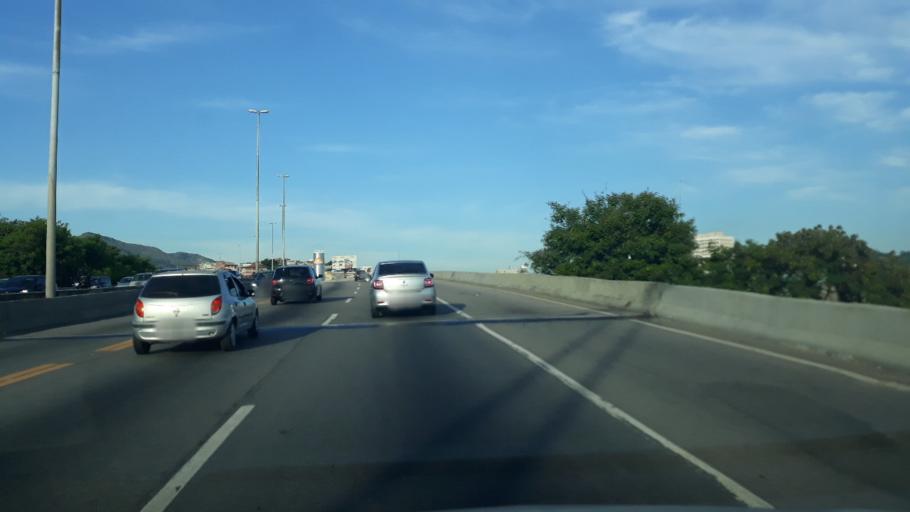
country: BR
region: Rio de Janeiro
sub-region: Rio De Janeiro
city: Rio de Janeiro
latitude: -22.8825
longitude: -43.2868
